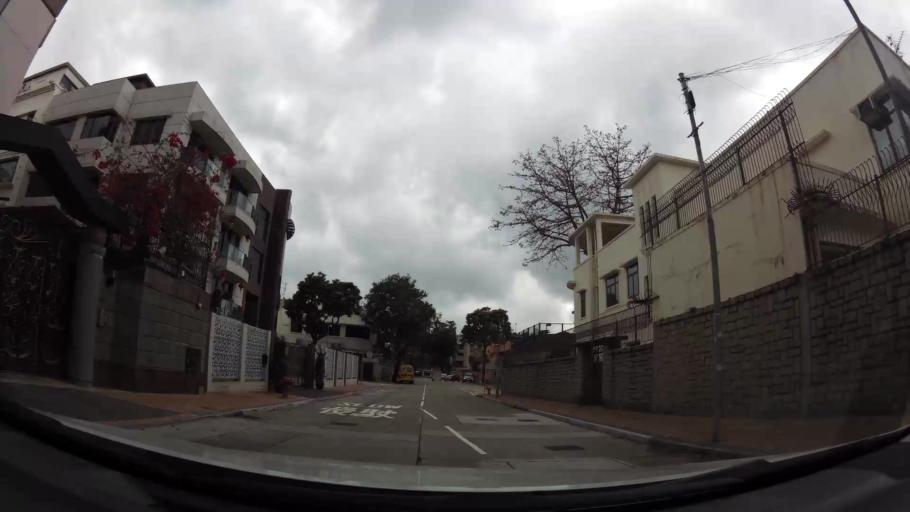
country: HK
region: Kowloon City
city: Kowloon
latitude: 22.3328
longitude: 114.1809
